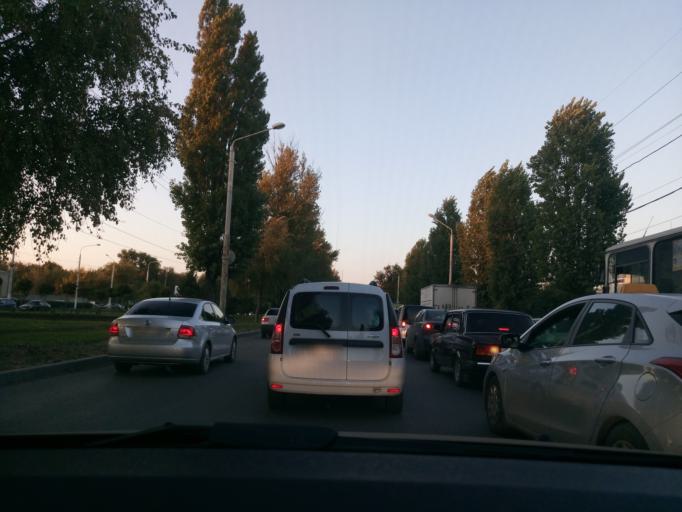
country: RU
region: Rostov
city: Kalinin
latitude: 47.2393
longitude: 39.6140
